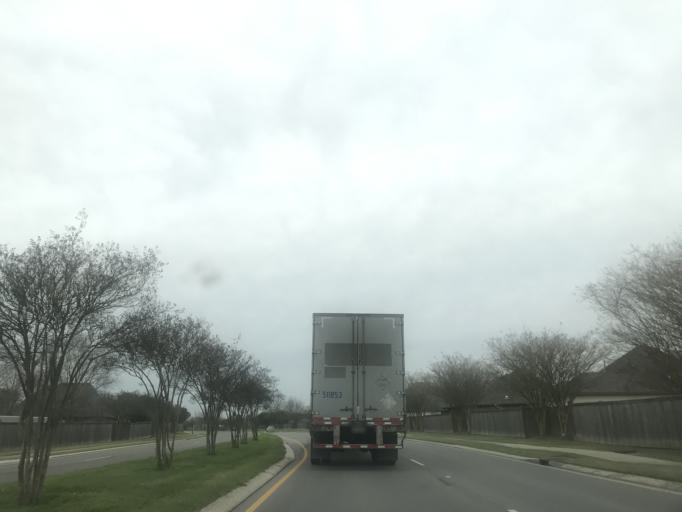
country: US
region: Louisiana
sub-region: East Baton Rouge Parish
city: Gardere
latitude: 30.3423
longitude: -91.1111
